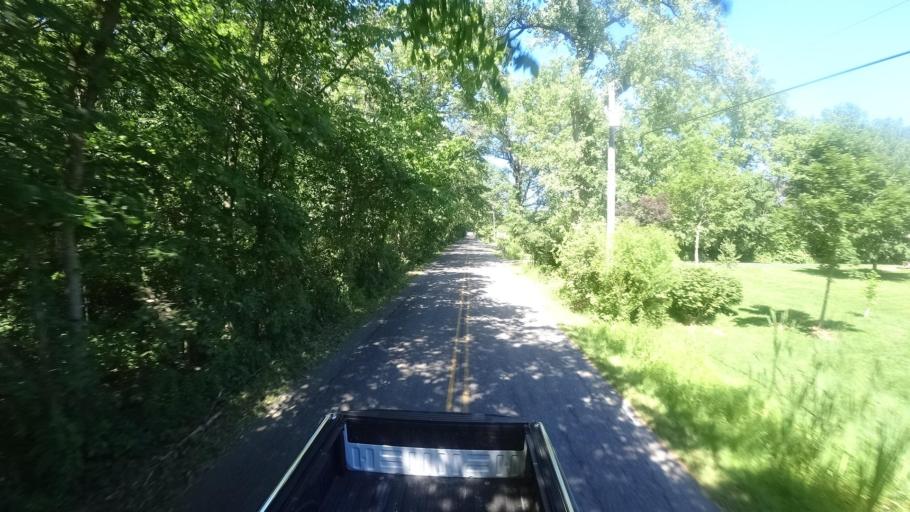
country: US
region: Indiana
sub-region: Porter County
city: Porter
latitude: 41.6297
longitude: -87.0815
